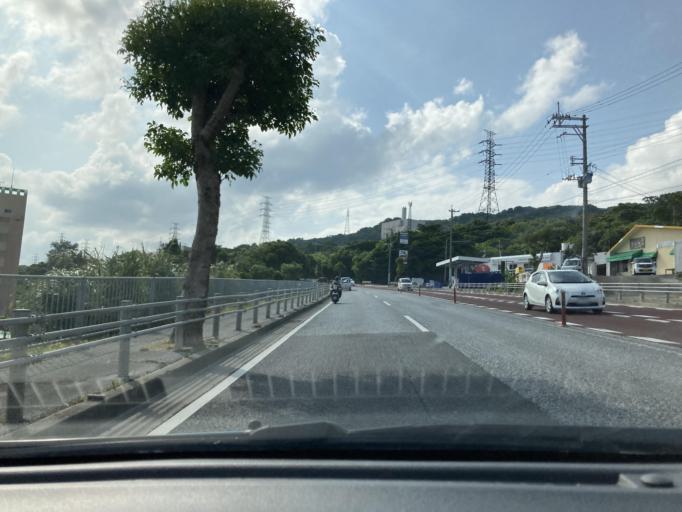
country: JP
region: Okinawa
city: Ginowan
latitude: 26.2783
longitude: 127.8041
